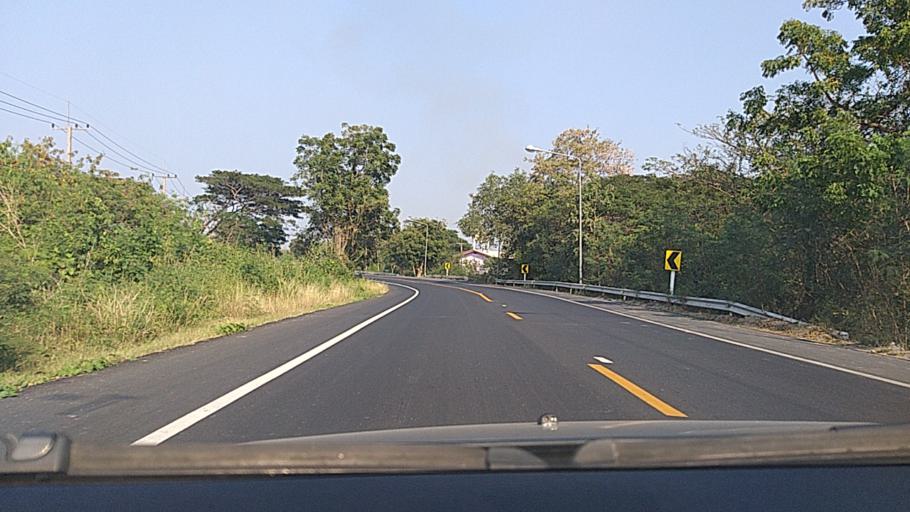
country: TH
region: Sing Buri
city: Phrom Buri
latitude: 14.7610
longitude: 100.4373
